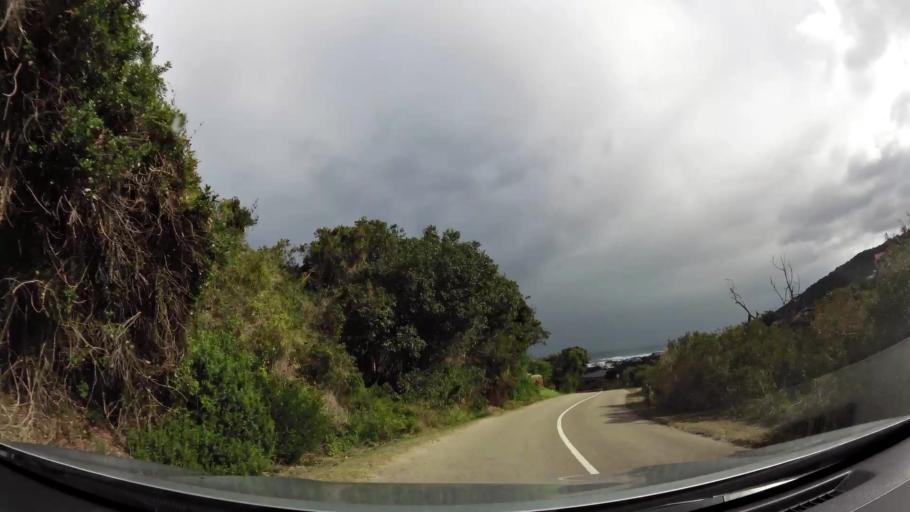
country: ZA
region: Western Cape
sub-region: Eden District Municipality
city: George
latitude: -34.0479
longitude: 22.3167
